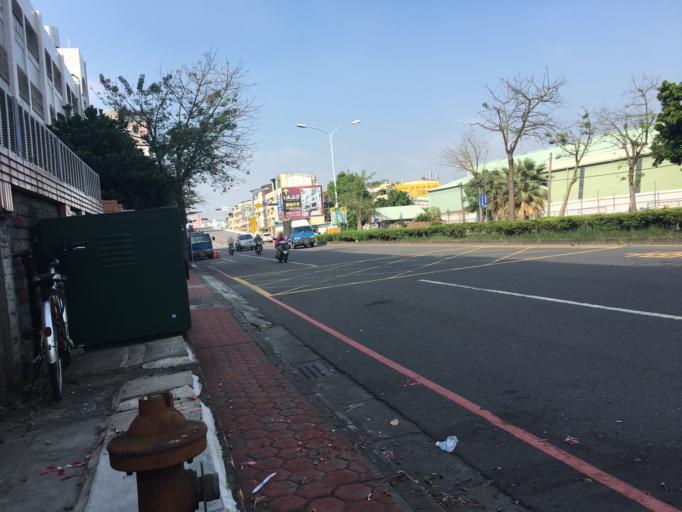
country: TW
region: Taiwan
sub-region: Changhua
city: Chang-hua
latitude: 24.0864
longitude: 120.5518
